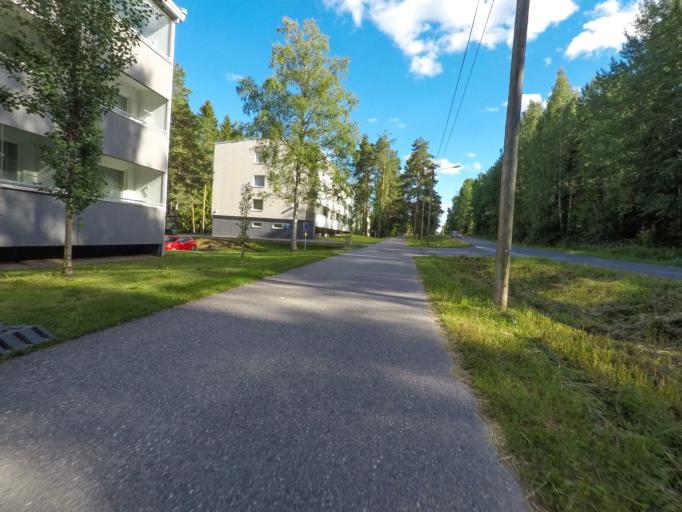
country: FI
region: South Karelia
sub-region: Lappeenranta
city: Lappeenranta
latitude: 61.0836
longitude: 28.1477
